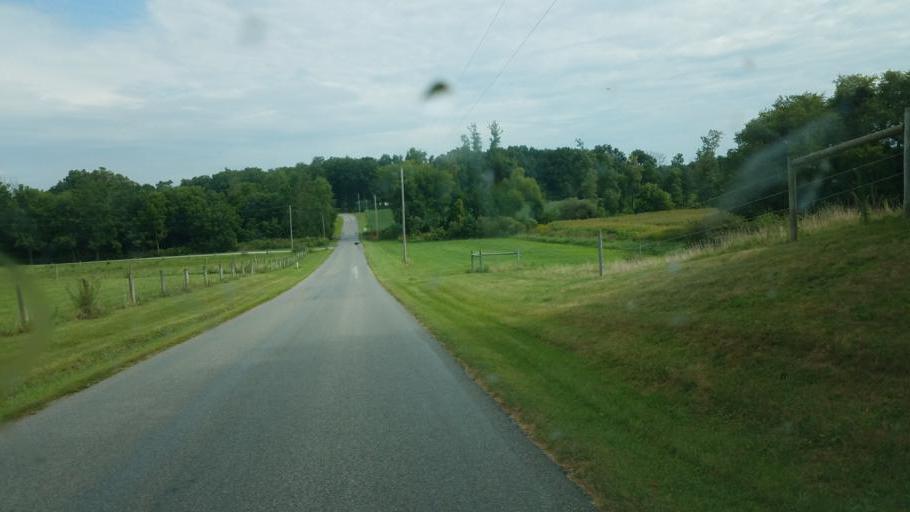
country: US
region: Ohio
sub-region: Knox County
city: Fredericktown
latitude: 40.4532
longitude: -82.6776
